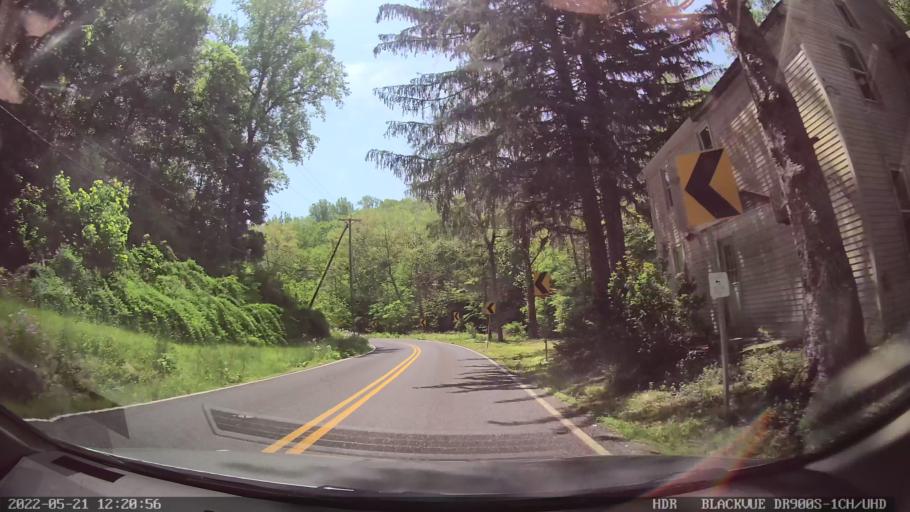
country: US
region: Pennsylvania
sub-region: Berks County
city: Bally
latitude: 40.4088
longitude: -75.6162
